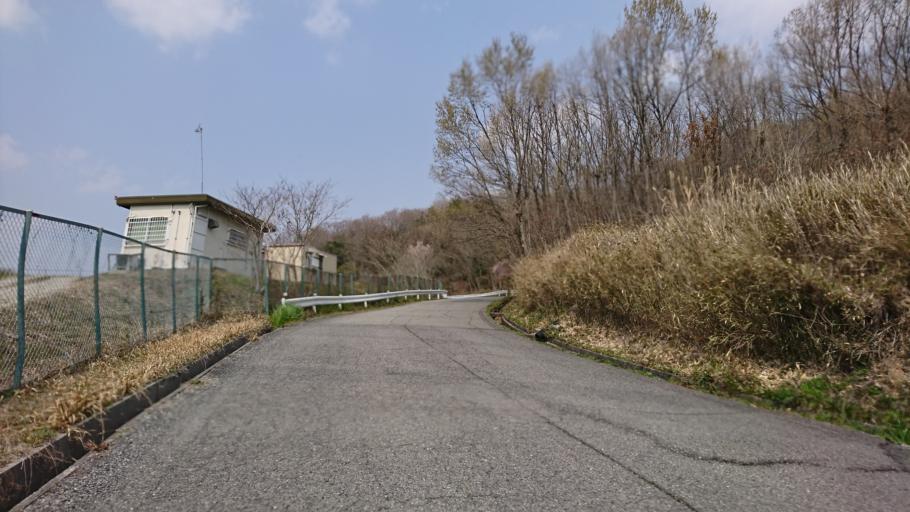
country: JP
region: Hyogo
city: Ono
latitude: 34.8229
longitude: 134.9040
